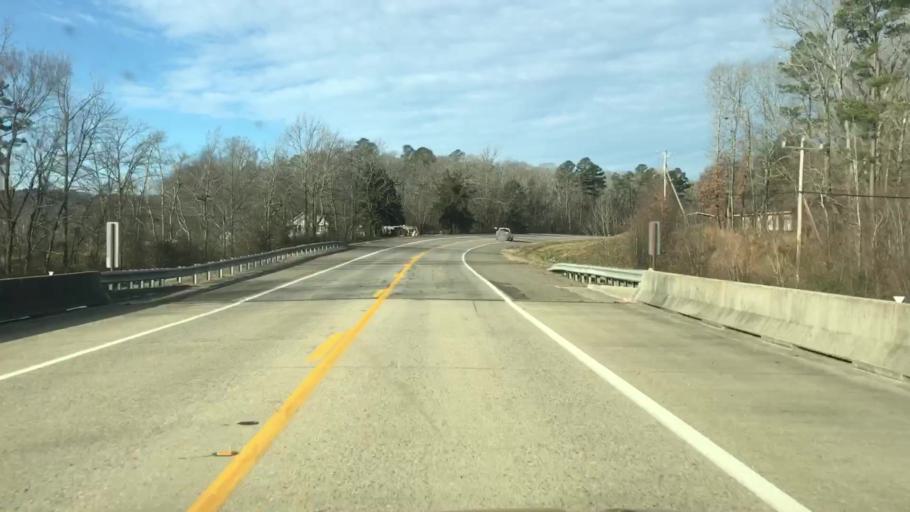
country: US
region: Arkansas
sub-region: Montgomery County
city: Mount Ida
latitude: 34.5393
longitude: -93.6011
